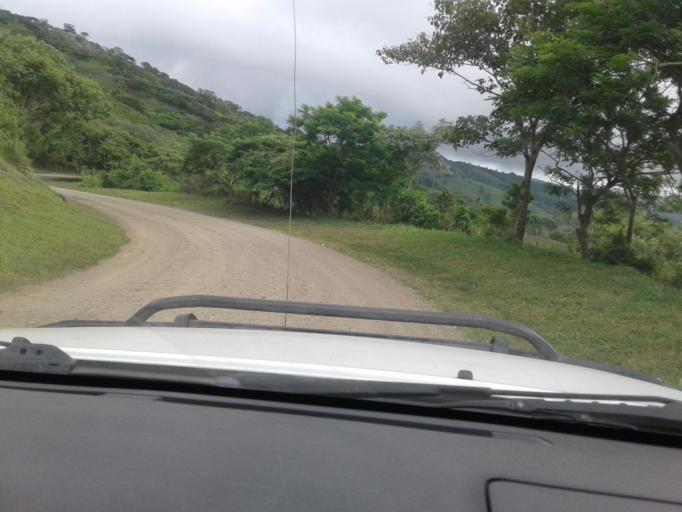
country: NI
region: Matagalpa
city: San Ramon
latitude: 12.9016
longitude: -85.8017
